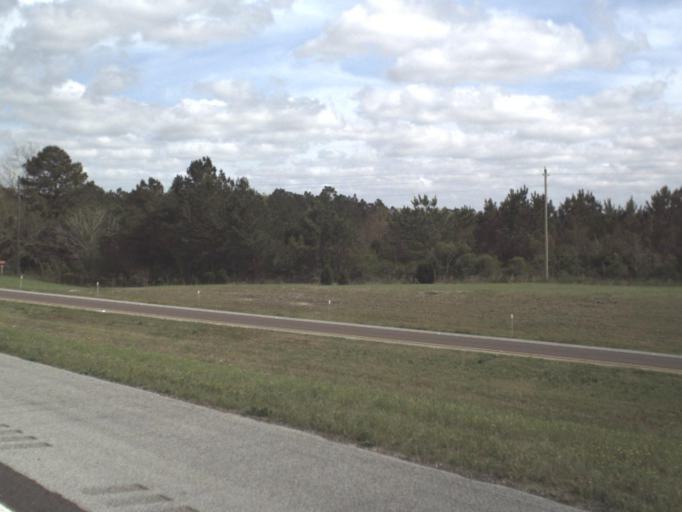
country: US
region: Florida
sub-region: Walton County
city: DeFuniak Springs
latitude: 30.6919
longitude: -86.1205
